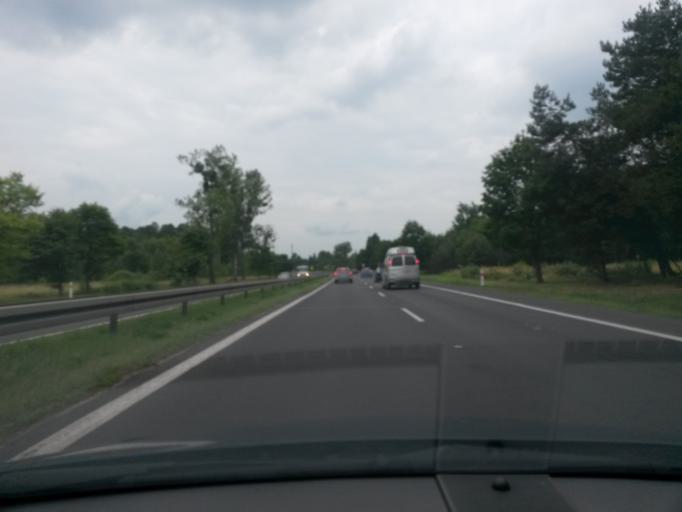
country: PL
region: Lodz Voivodeship
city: Zabia Wola
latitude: 52.0460
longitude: 20.7069
